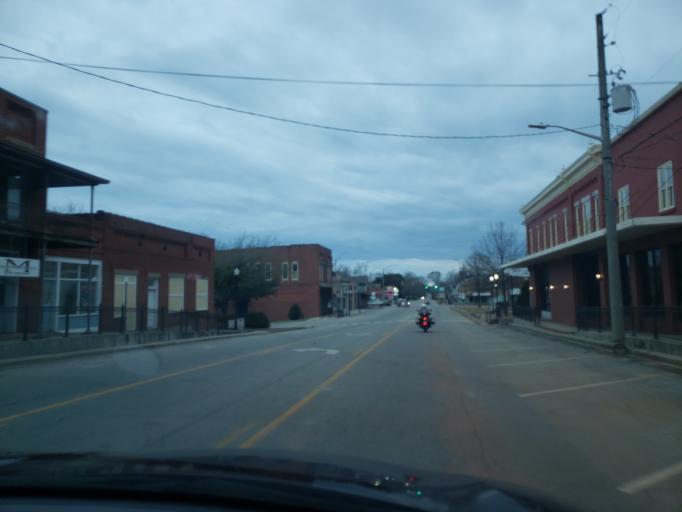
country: US
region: Alabama
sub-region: Chambers County
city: Lafayette
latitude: 32.8985
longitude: -85.4012
